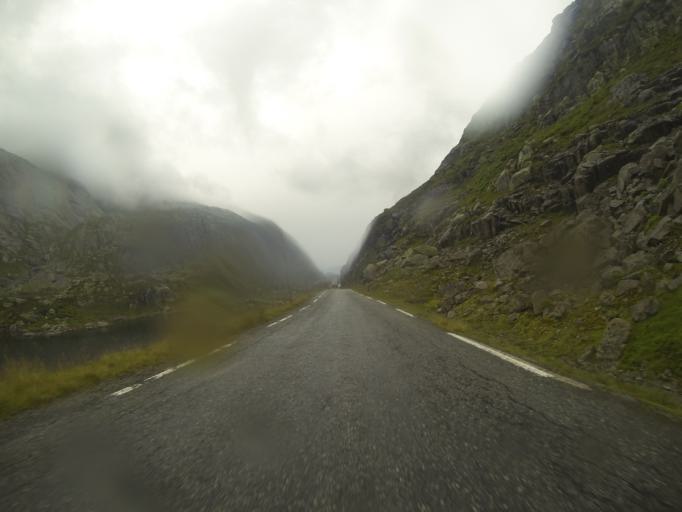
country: NO
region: Hordaland
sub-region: Odda
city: Odda
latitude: 59.7618
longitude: 6.7211
